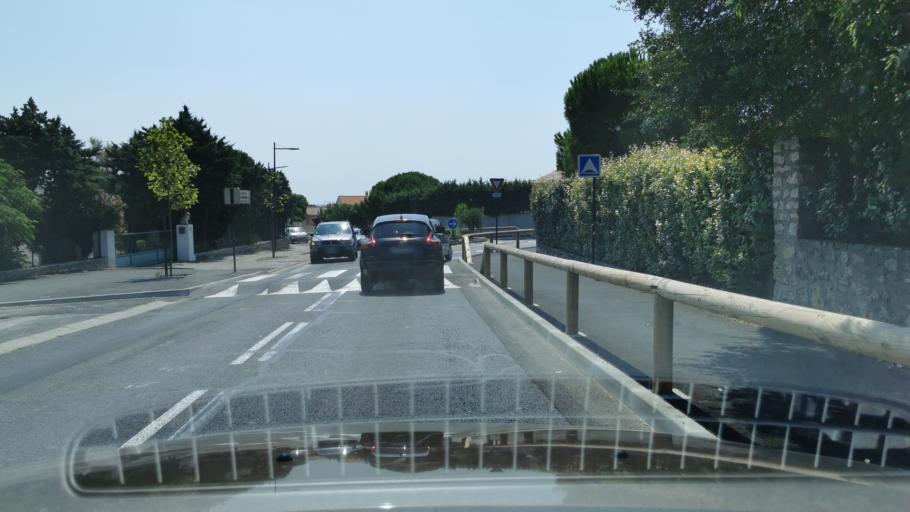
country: FR
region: Languedoc-Roussillon
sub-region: Departement de l'Aude
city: Leucate
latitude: 42.9069
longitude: 3.0335
